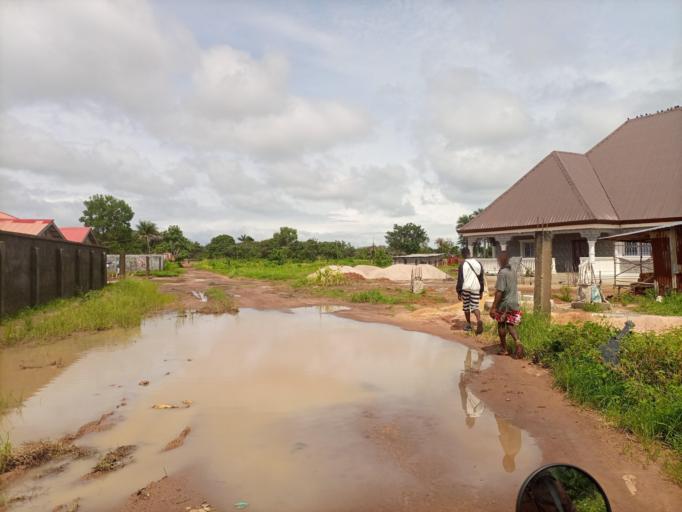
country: SL
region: Northern Province
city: Masoyila
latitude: 8.6139
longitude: -13.1742
